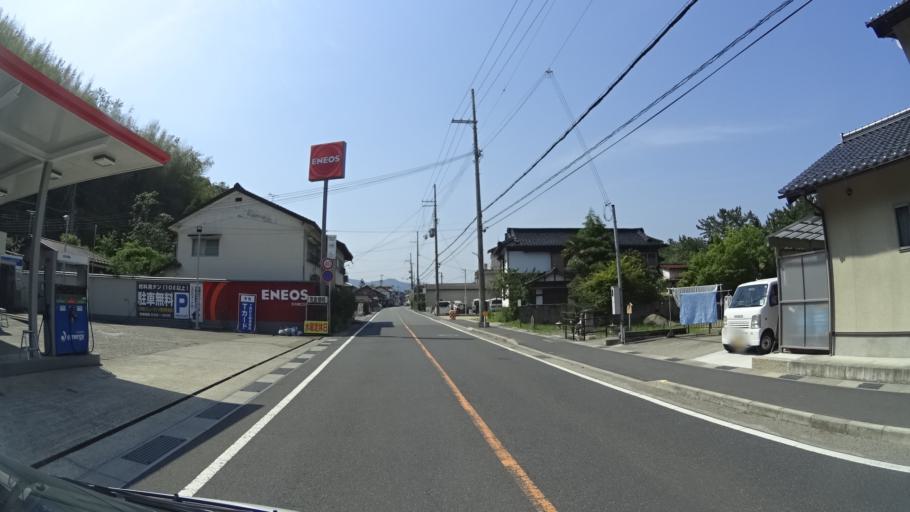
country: JP
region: Kyoto
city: Miyazu
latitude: 35.5549
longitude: 135.1868
